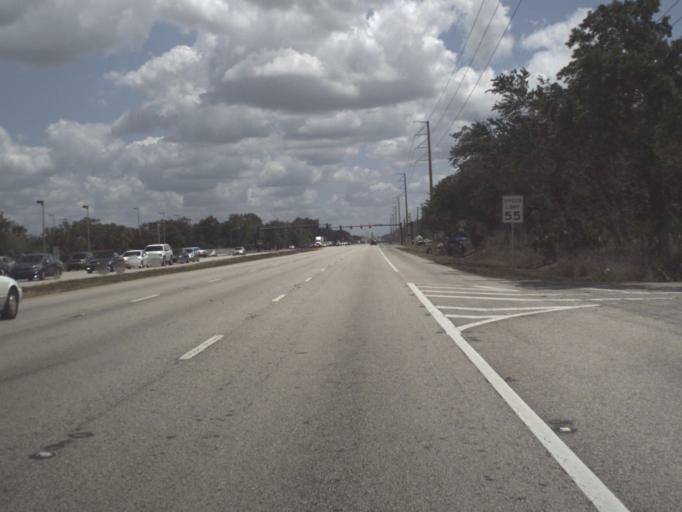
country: US
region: Florida
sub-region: Orange County
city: Sky Lake
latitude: 28.4507
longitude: -81.3876
